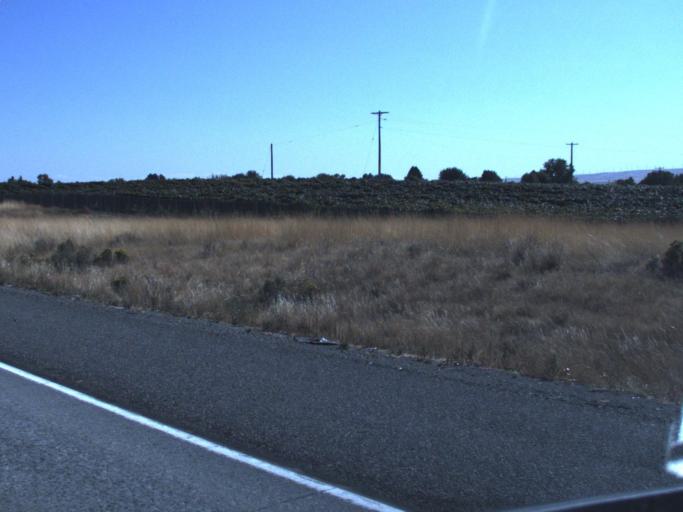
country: US
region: Washington
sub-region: Franklin County
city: West Pasco
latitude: 46.2535
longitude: -119.1436
